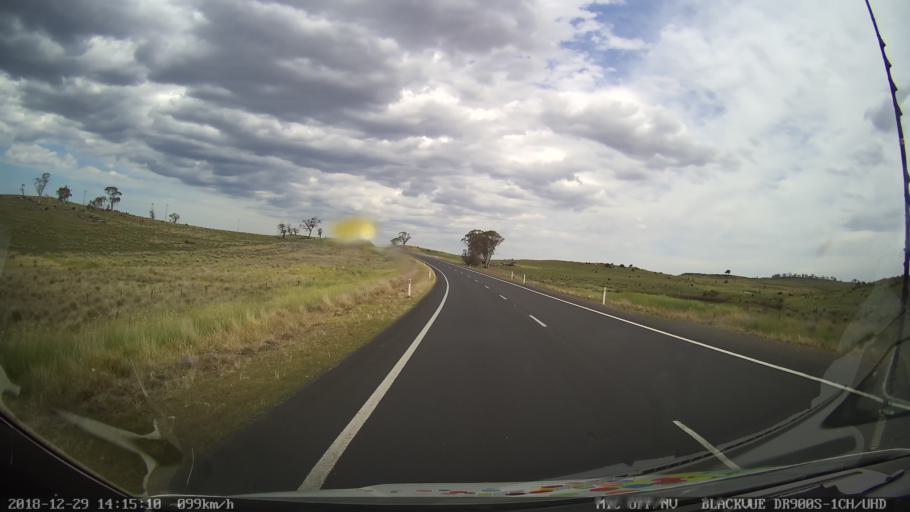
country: AU
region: New South Wales
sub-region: Cooma-Monaro
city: Cooma
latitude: -36.4524
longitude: 149.2383
